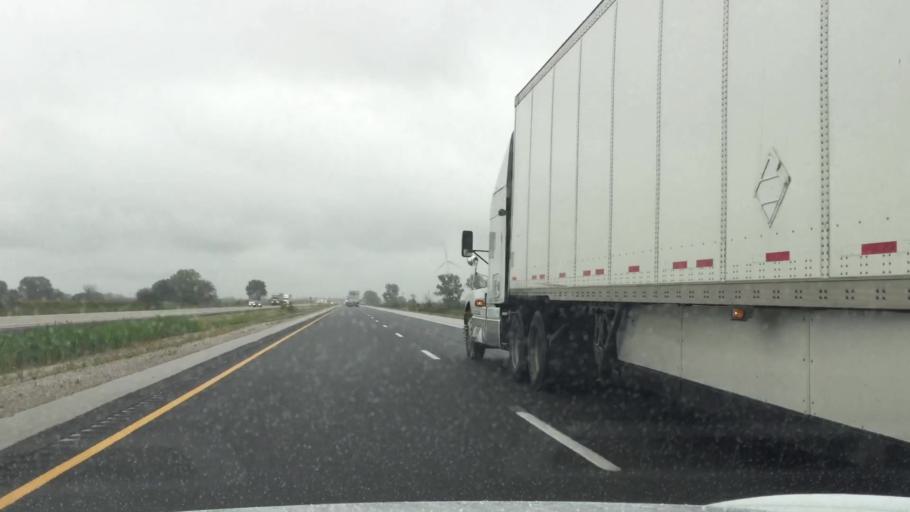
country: CA
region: Ontario
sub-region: Lambton County
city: Walpole Island
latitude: 42.3237
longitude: -82.2501
